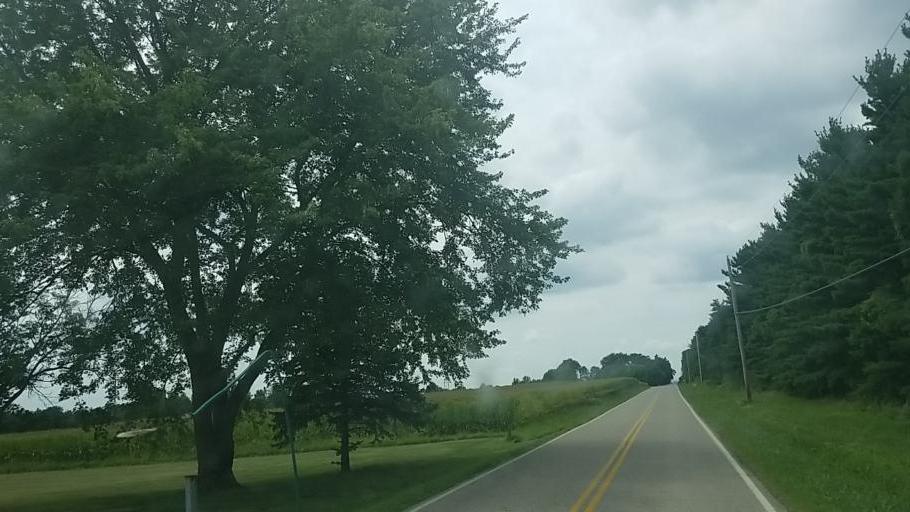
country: US
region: Ohio
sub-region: Fairfield County
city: Lithopolis
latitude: 39.7526
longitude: -82.8567
